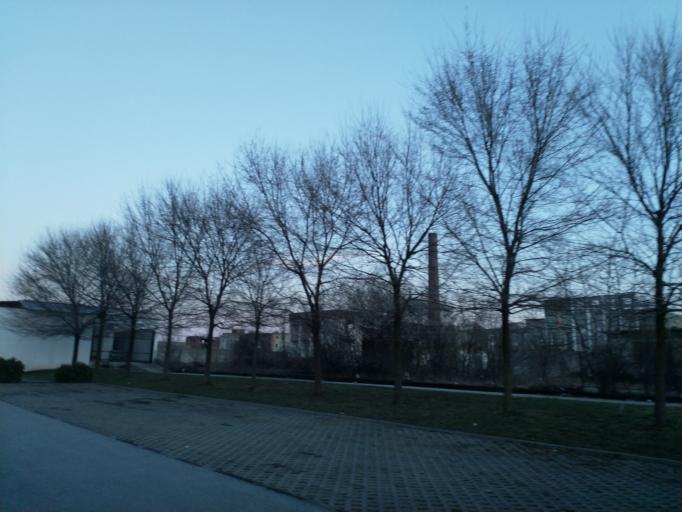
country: RS
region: Central Serbia
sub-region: Pomoravski Okrug
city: Cuprija
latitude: 43.9176
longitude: 21.3781
